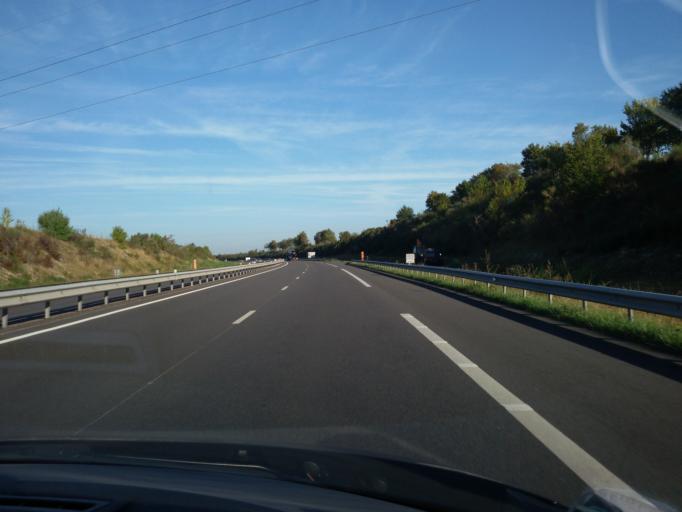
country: FR
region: Centre
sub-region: Departement du Cher
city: Trouy
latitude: 47.0337
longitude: 2.3714
